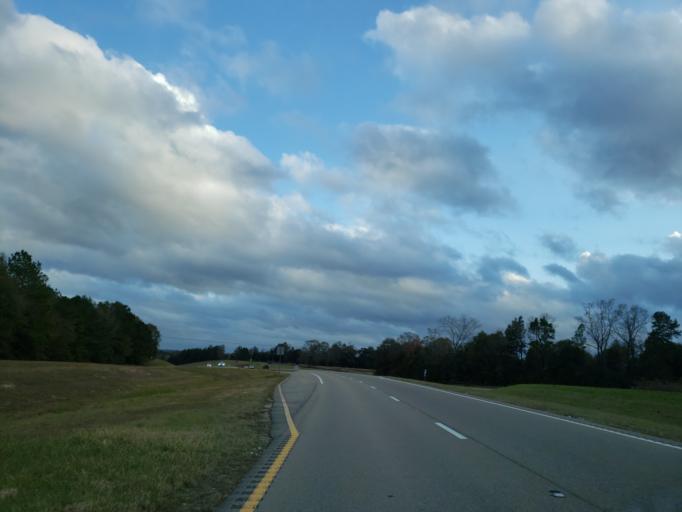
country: US
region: Mississippi
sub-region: George County
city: Lucedale
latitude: 31.0208
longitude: -88.7162
